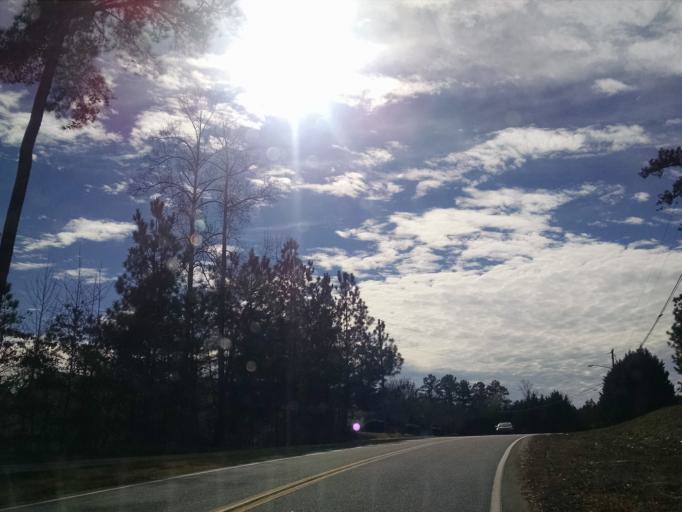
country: US
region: Georgia
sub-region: Gwinnett County
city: Sugar Hill
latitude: 34.1282
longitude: -84.0633
